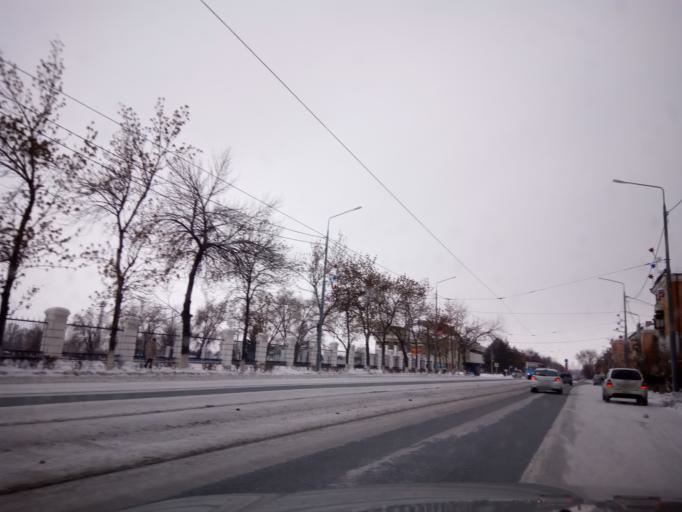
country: RU
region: Orenburg
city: Novotroitsk
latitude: 51.1957
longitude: 58.3269
